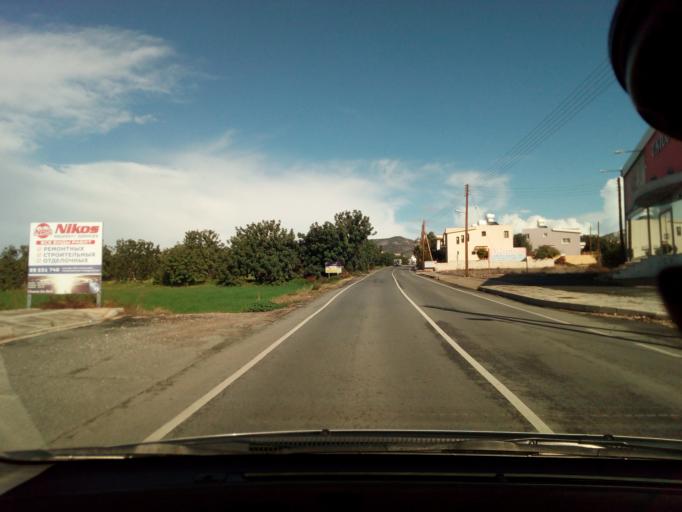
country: CY
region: Pafos
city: Mesogi
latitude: 34.8055
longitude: 32.4495
